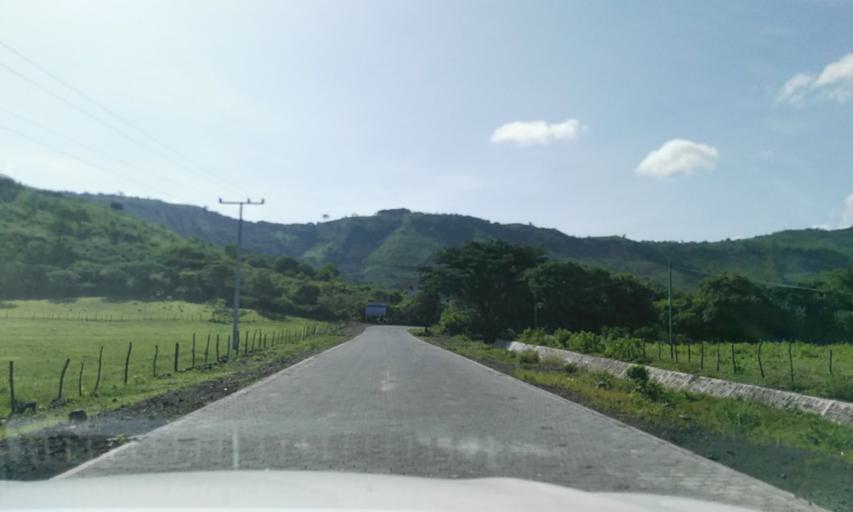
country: NI
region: Matagalpa
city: Terrabona
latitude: 12.7384
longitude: -85.9694
